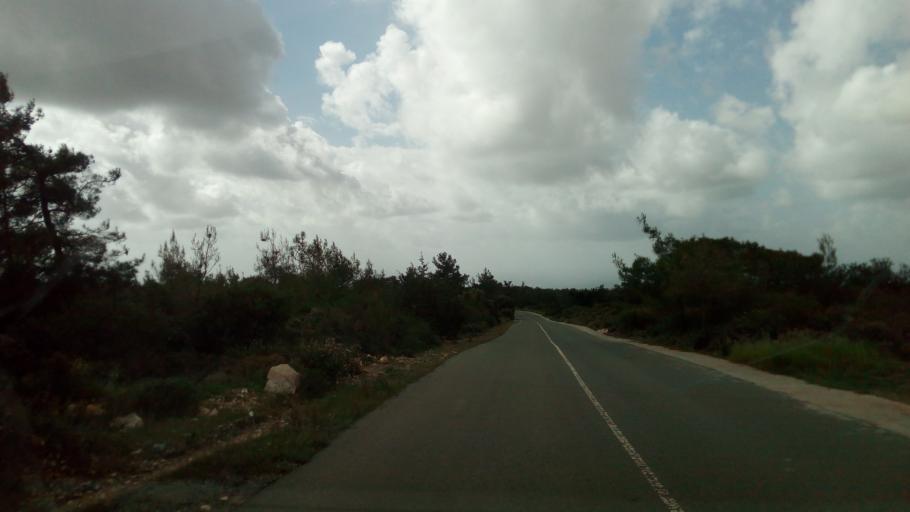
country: CY
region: Limassol
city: Sotira
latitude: 34.7261
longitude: 32.8657
